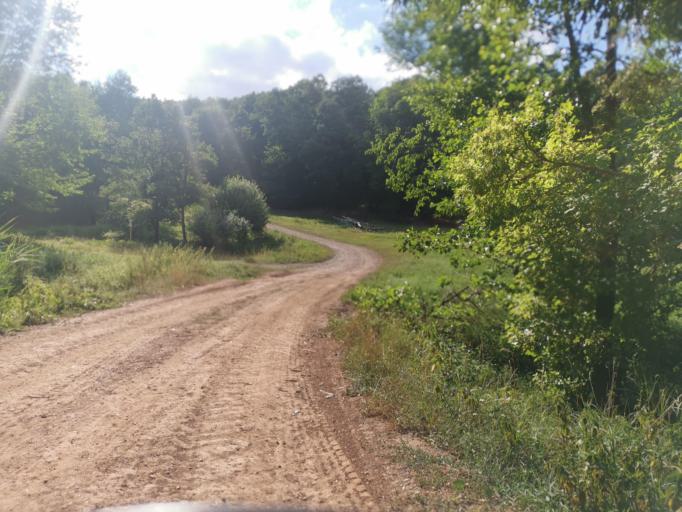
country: SK
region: Trnavsky
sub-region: Okres Senica
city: Senica
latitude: 48.7817
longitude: 17.3507
